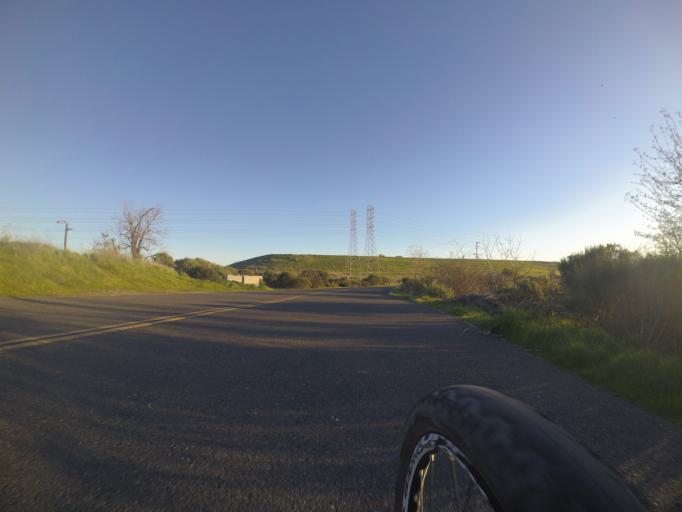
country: US
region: California
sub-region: Santa Clara County
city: Milpitas
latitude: 37.4363
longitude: -121.9579
